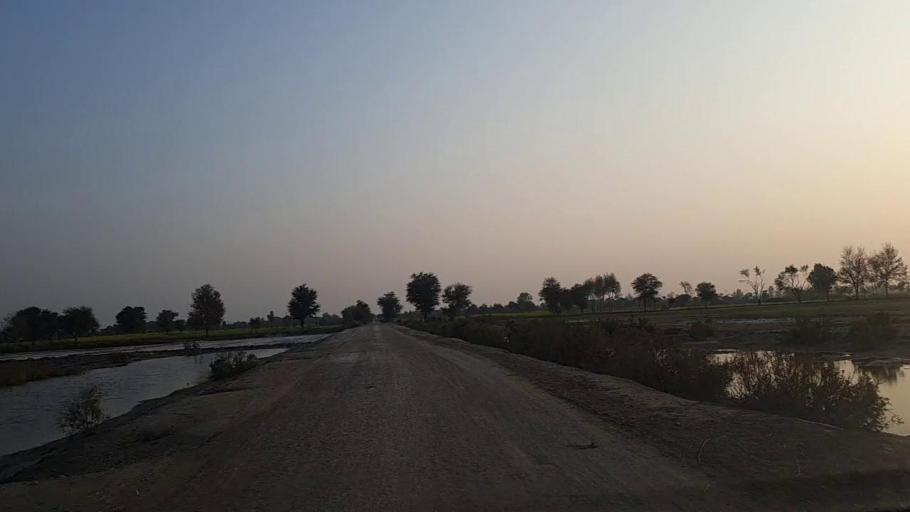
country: PK
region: Sindh
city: Daur
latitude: 26.4203
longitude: 68.3678
